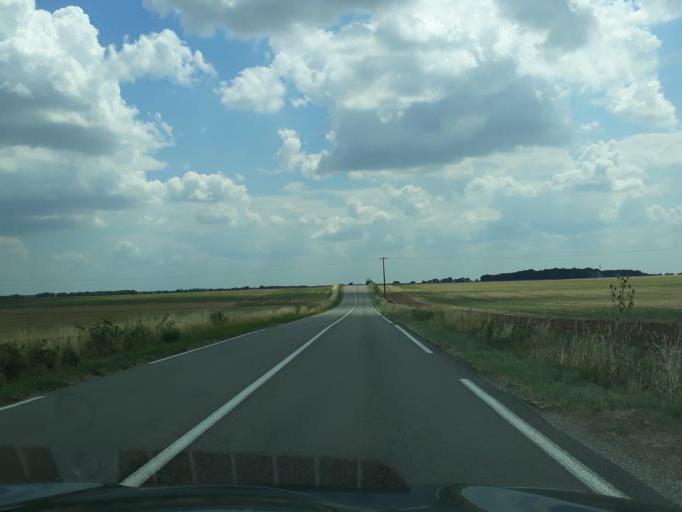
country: FR
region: Centre
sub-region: Departement du Cher
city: Saint-Germain-du-Puy
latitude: 47.0631
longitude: 2.5171
